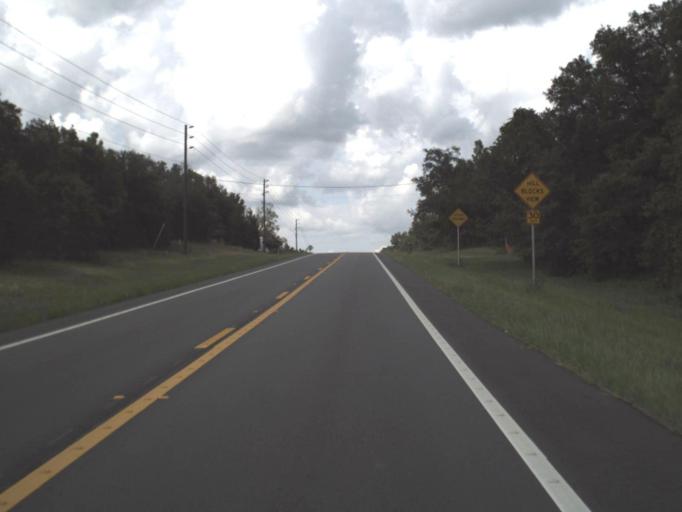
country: US
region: Florida
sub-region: Citrus County
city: Floral City
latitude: 28.6986
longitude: -82.3158
